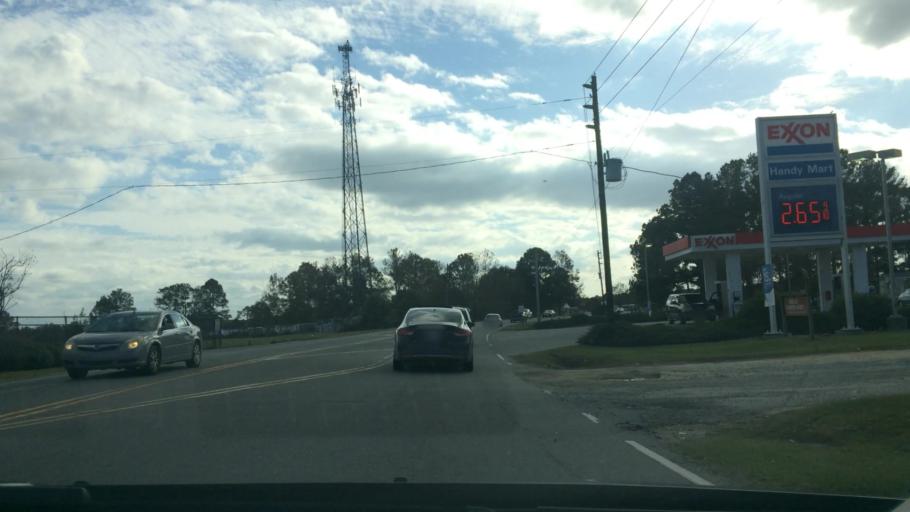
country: US
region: North Carolina
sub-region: Wayne County
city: Elroy
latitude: 35.4046
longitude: -77.8980
